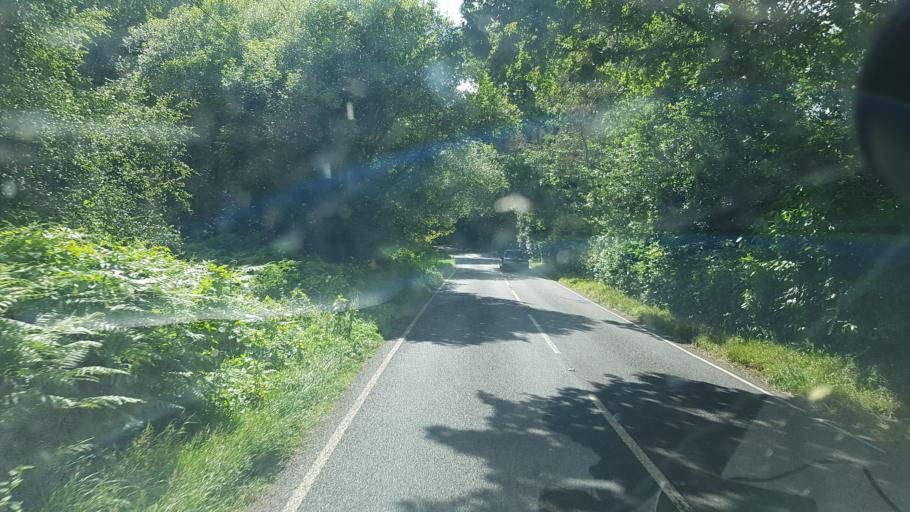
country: GB
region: England
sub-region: West Sussex
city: Broadfield
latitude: 51.0630
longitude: -0.1838
